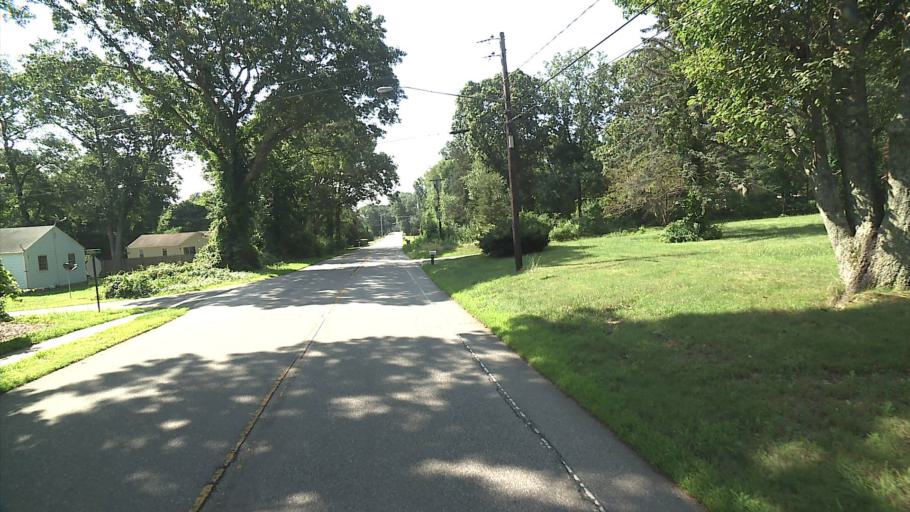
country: US
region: Connecticut
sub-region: Middlesex County
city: Clinton
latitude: 41.2802
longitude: -72.4865
